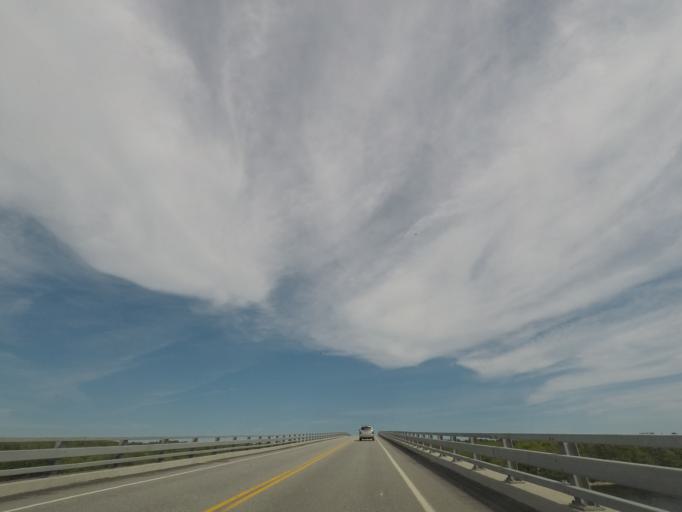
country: US
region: Maine
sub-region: Sagadahoc County
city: Richmond
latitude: 44.0902
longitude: -69.7823
